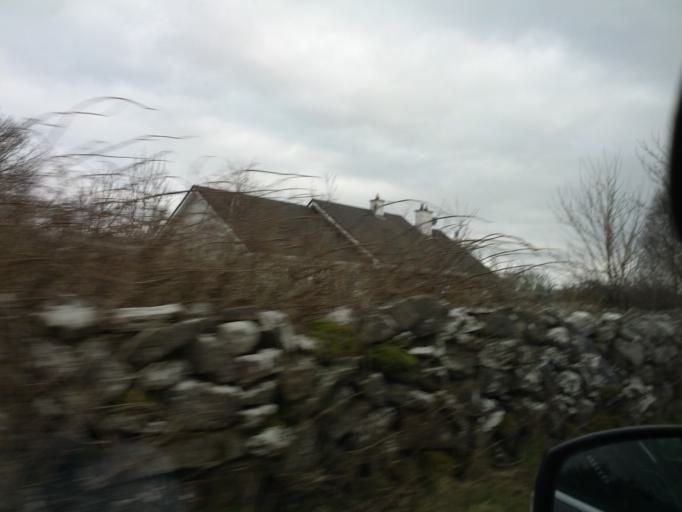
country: IE
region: Connaught
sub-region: County Galway
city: Oranmore
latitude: 53.1644
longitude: -8.8784
